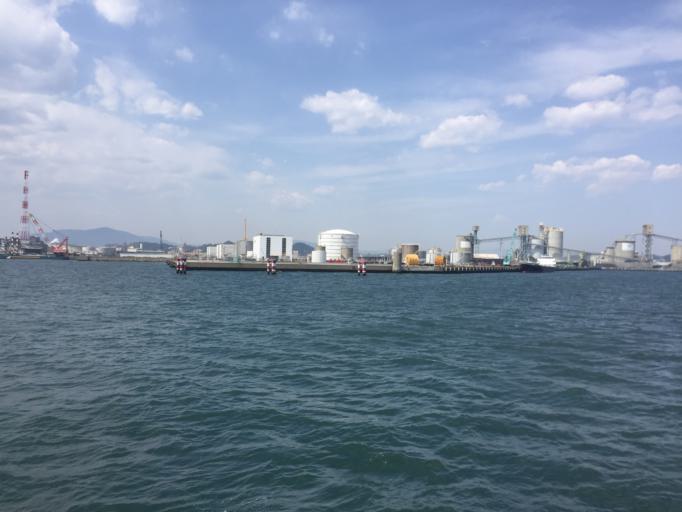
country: JP
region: Fukushima
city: Iwaki
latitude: 36.9352
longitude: 140.8926
